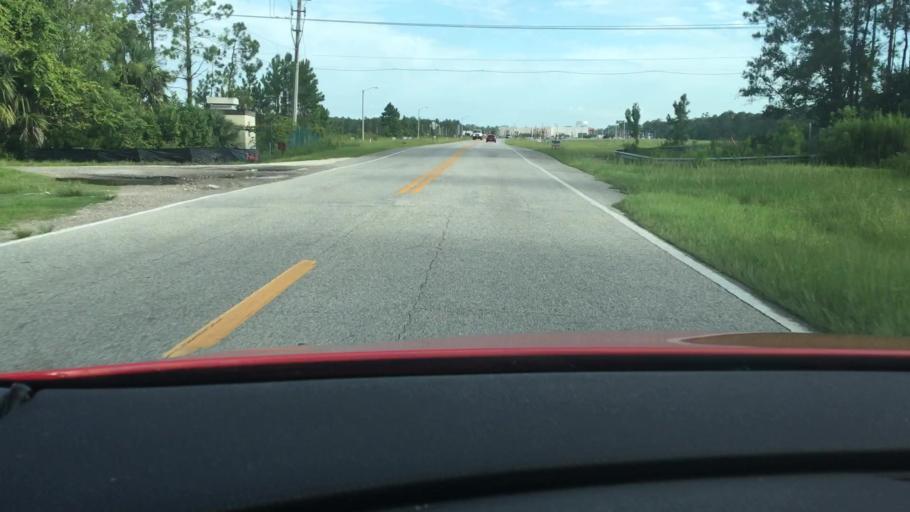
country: US
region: Florida
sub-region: Volusia County
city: Daytona Beach
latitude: 29.1834
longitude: -81.0928
